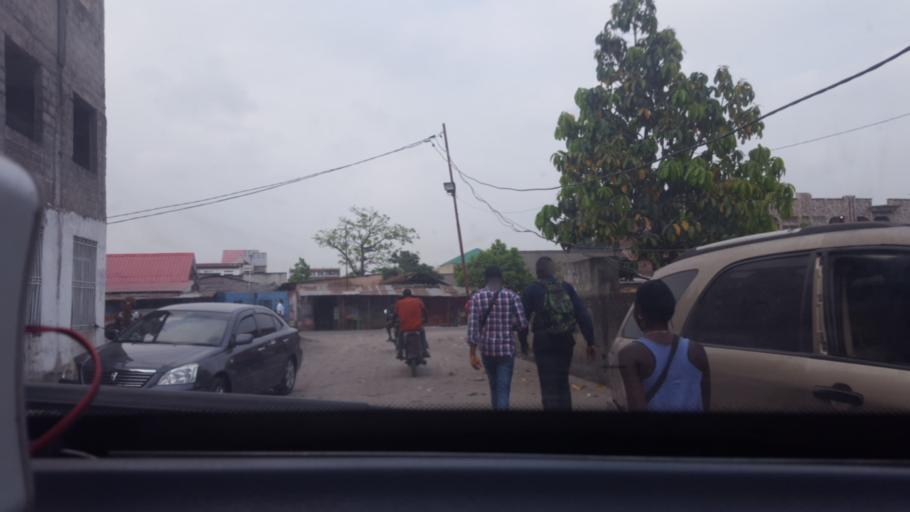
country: CD
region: Kinshasa
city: Kinshasa
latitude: -4.3346
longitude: 15.3169
